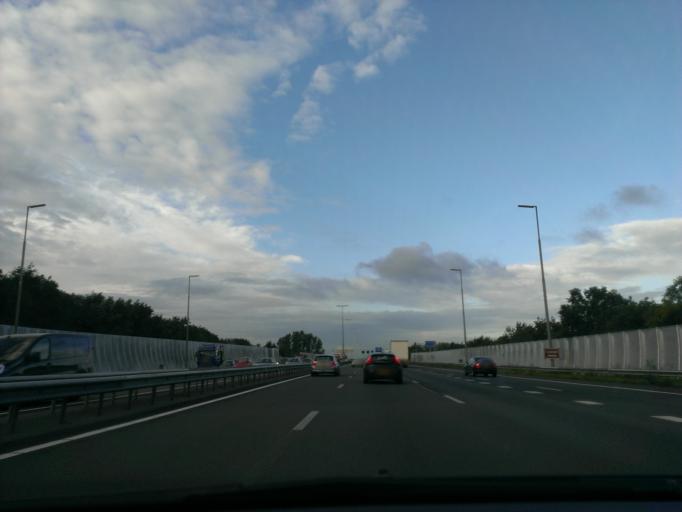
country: NL
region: Gelderland
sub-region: Gemeente Hattem
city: Hattem
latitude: 52.5027
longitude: 6.0596
